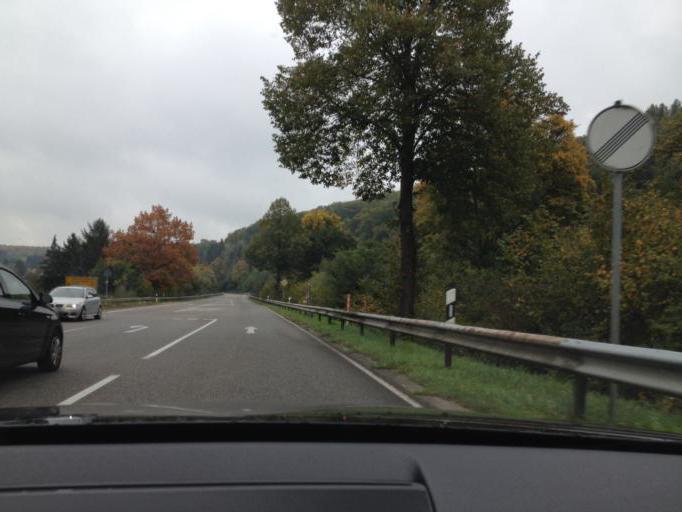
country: DE
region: Rheinland-Pfalz
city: Dellfeld
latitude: 49.2304
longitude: 7.4632
